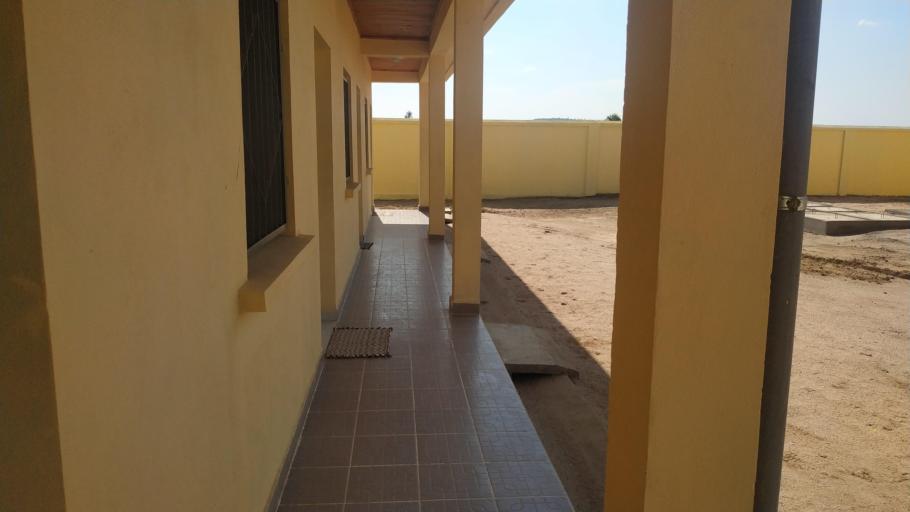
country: MG
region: Analamanga
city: Anjozorobe
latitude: -18.2760
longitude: 48.2626
